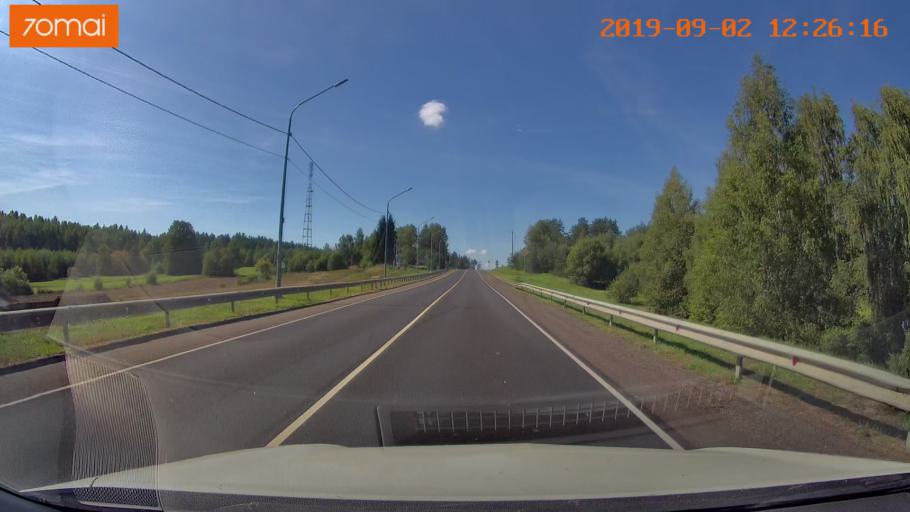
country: RU
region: Smolensk
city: Shumyachi
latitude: 53.8576
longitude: 32.5694
